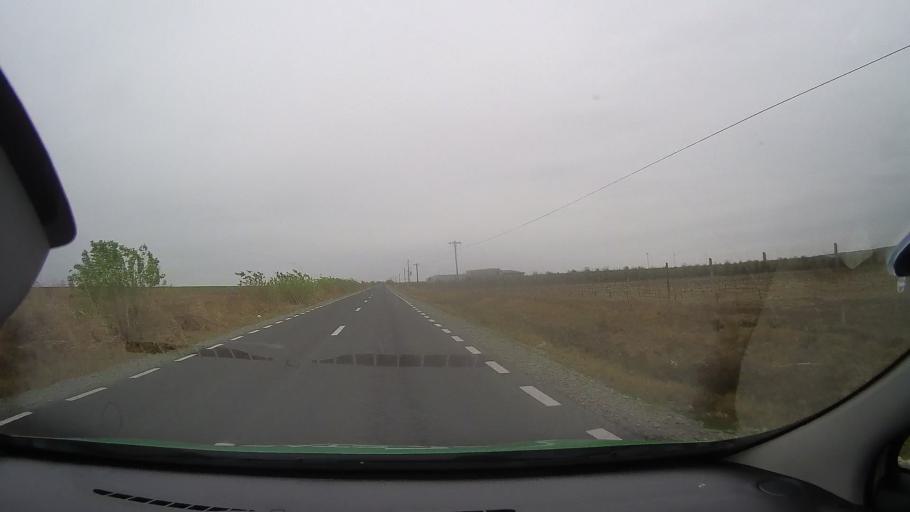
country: RO
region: Constanta
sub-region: Comuna Tortoman
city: Tortoman
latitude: 44.3654
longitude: 28.2086
